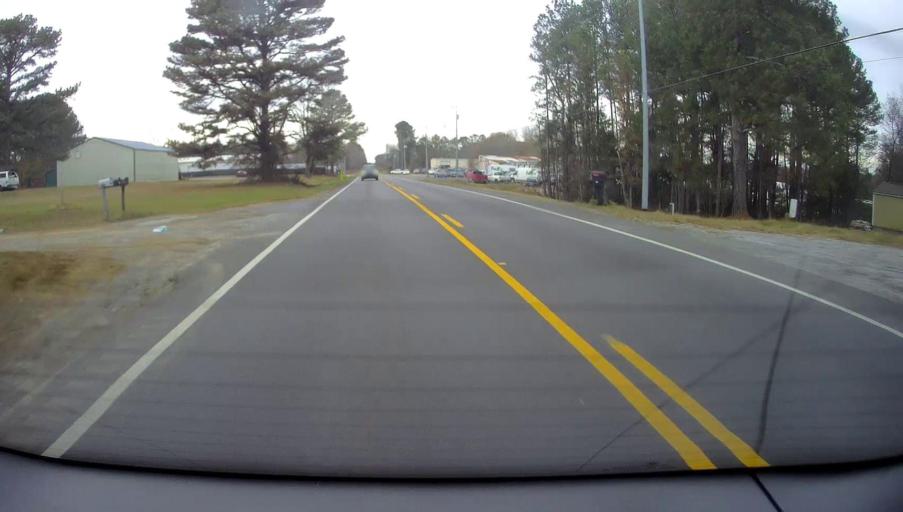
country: US
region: Alabama
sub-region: Morgan County
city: Priceville
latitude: 34.4942
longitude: -86.8440
